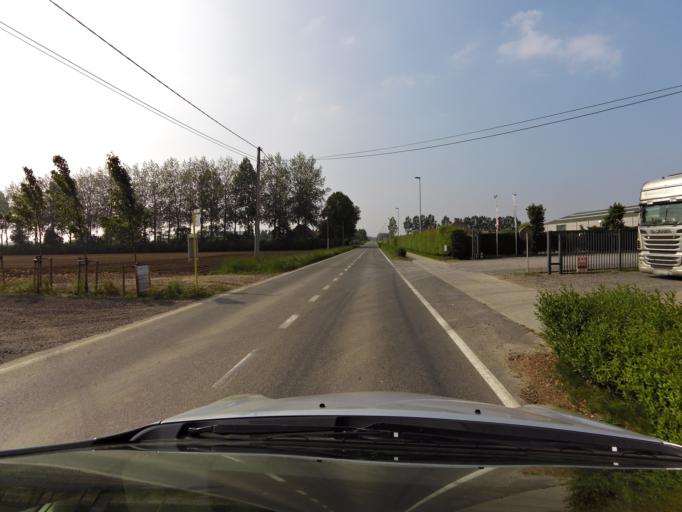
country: BE
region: Flanders
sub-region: Provincie West-Vlaanderen
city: Poperinge
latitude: 50.8660
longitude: 2.7165
